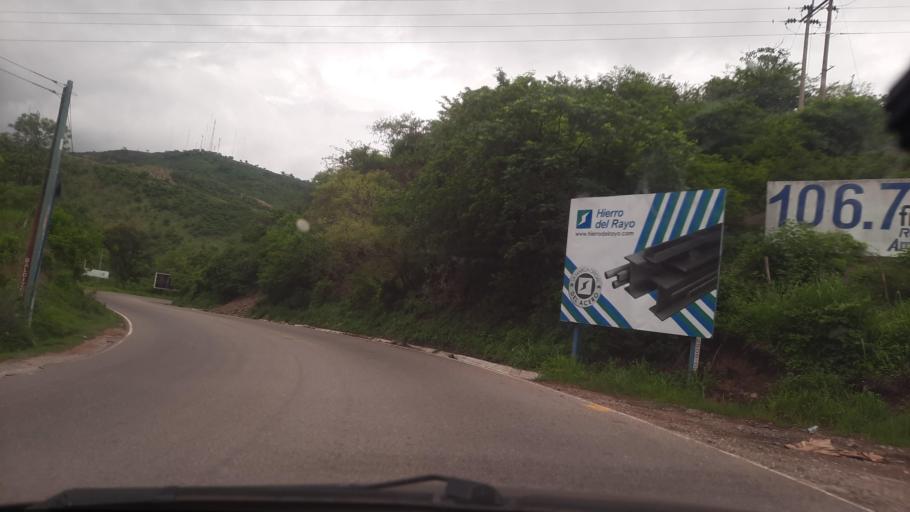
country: GT
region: Chiquimula
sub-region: Municipio de Chiquimula
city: Chiquimula
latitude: 14.8615
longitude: -89.5151
